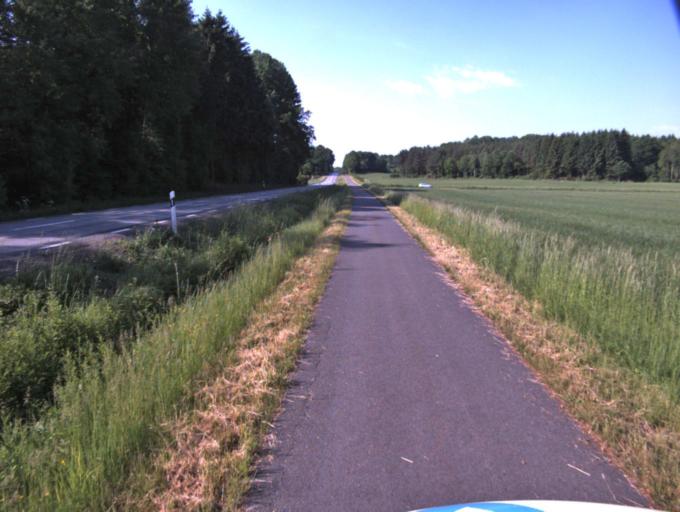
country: SE
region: Skane
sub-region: Kristianstads Kommun
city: Tollarp
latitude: 56.1604
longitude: 14.2729
